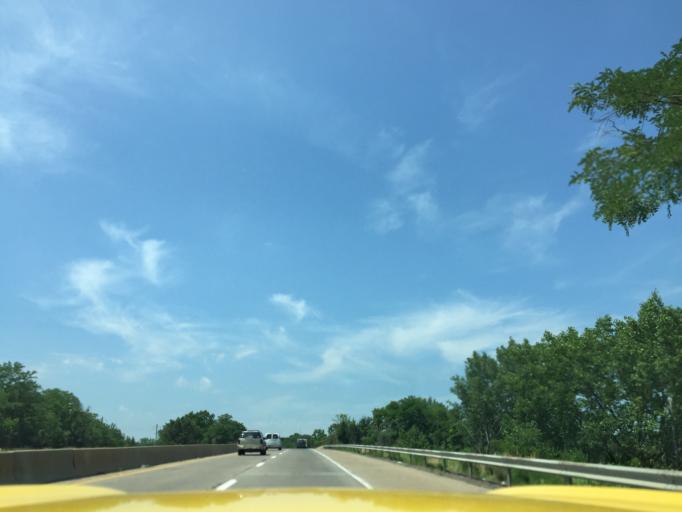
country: US
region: Pennsylvania
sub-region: Bucks County
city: Morrisville
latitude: 40.1950
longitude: -74.8136
